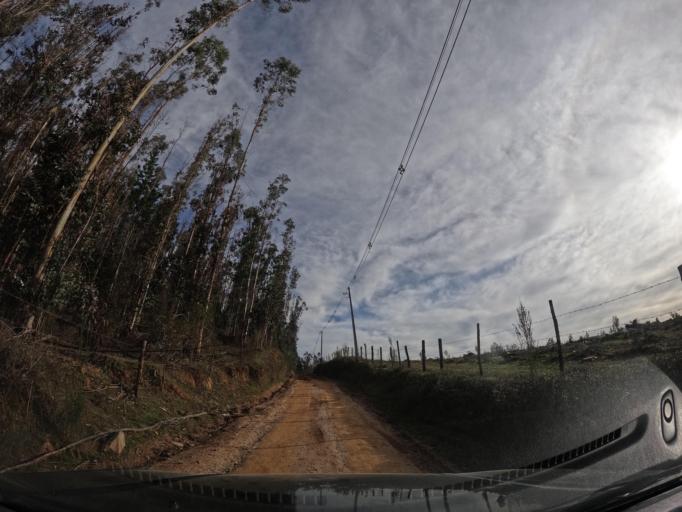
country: CL
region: Biobio
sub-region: Provincia de Concepcion
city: Chiguayante
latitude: -37.0212
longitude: -72.9155
